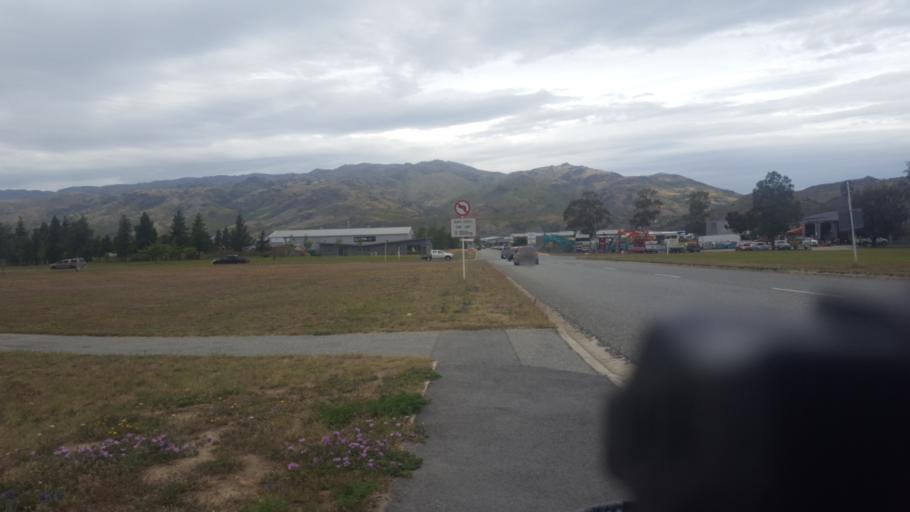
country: NZ
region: Otago
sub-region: Queenstown-Lakes District
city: Wanaka
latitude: -45.0490
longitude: 169.1831
